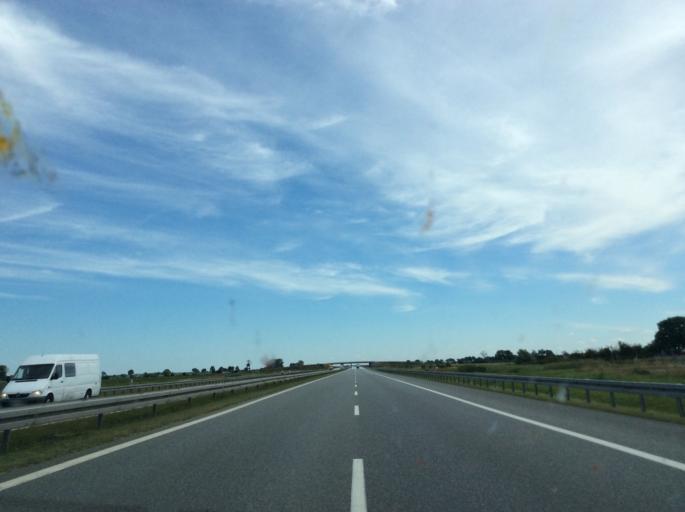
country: PL
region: Greater Poland Voivodeship
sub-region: Powiat nowotomyski
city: Kuslin
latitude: 52.3807
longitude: 16.3343
